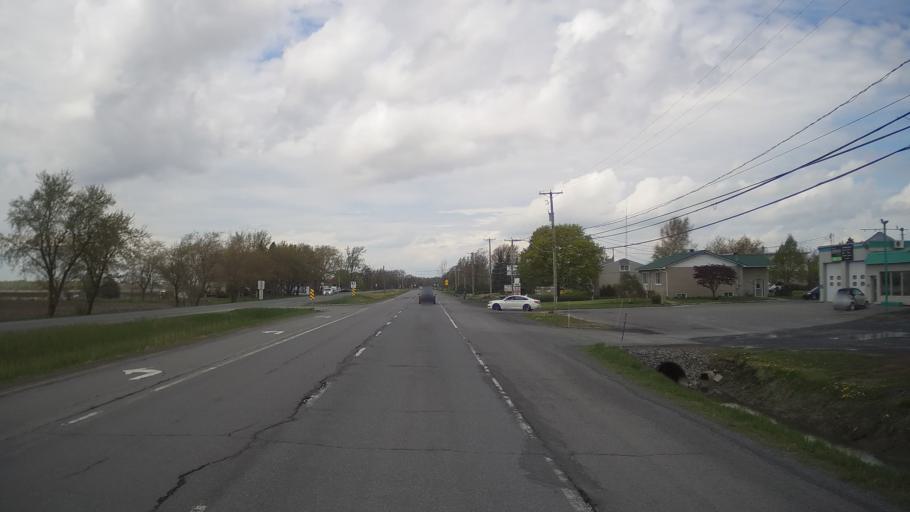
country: CA
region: Quebec
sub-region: Monteregie
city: Carignan
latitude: 45.3685
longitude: -73.3369
